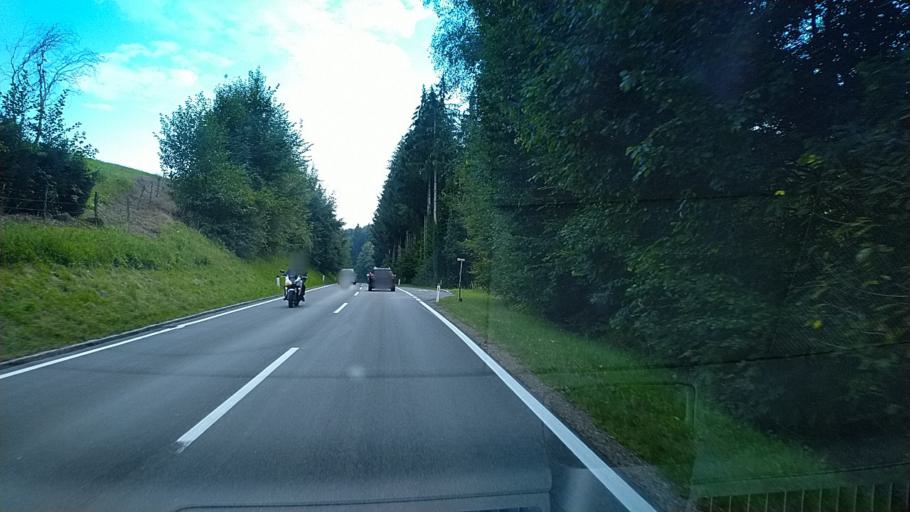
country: AT
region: Styria
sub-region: Politischer Bezirk Deutschlandsberg
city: Sankt Peter im Sulmtal
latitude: 46.7409
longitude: 15.2317
